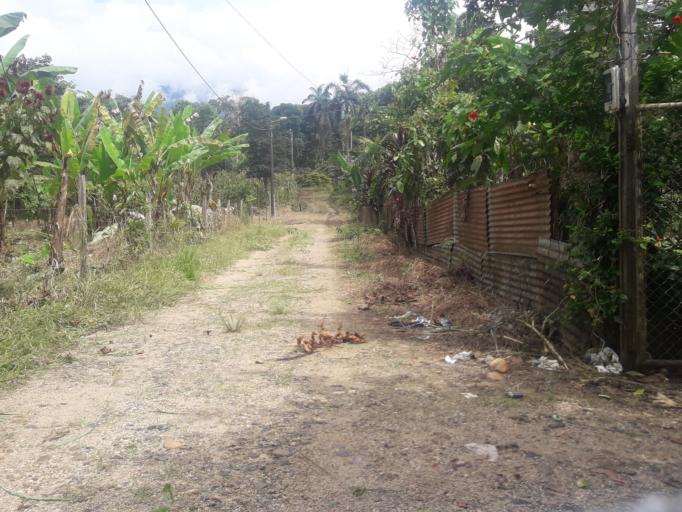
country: EC
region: Napo
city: Tena
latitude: -0.9783
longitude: -77.8475
